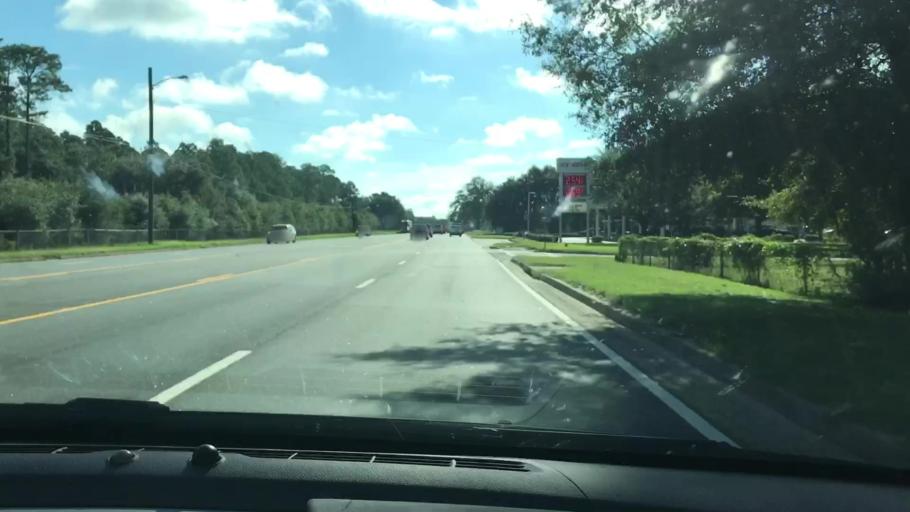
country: US
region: Georgia
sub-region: Dougherty County
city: Albany
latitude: 31.5799
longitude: -84.0923
